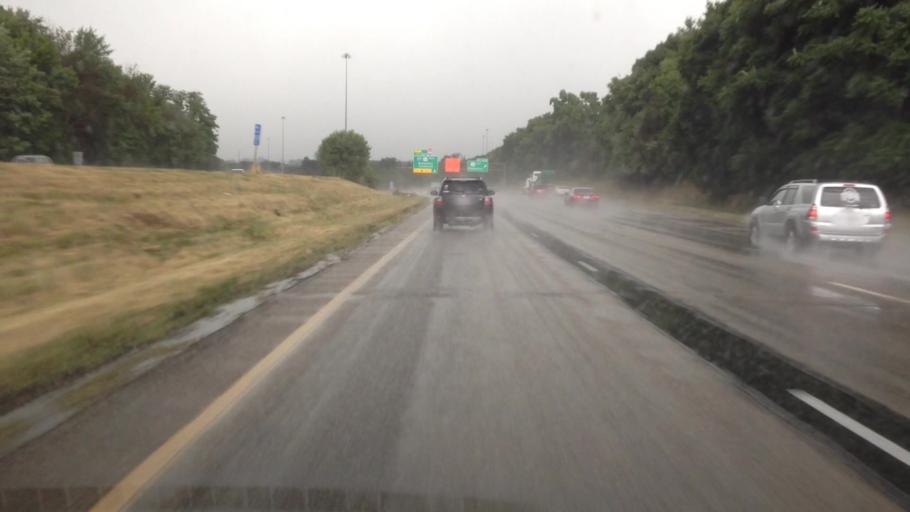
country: US
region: Ohio
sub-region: Summit County
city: Portage Lakes
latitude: 41.0187
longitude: -81.4966
